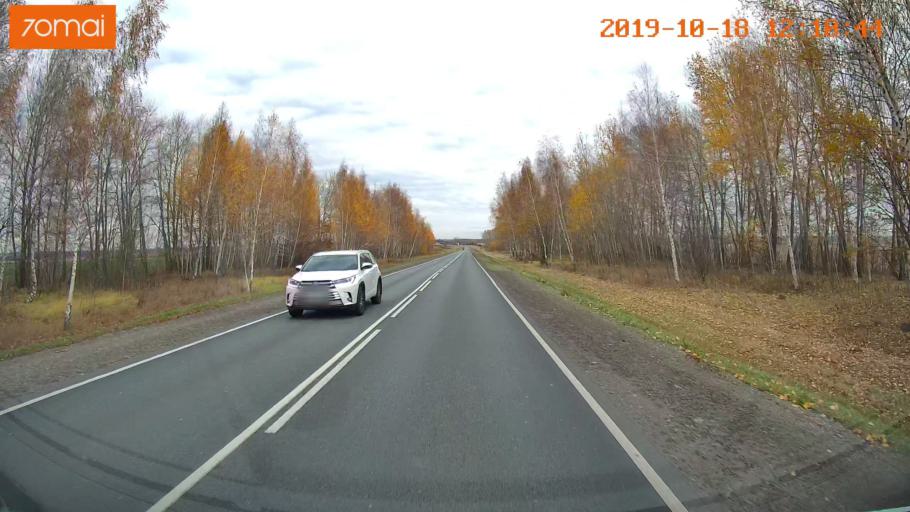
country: RU
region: Rjazan
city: Zakharovo
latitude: 54.3949
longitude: 39.3373
